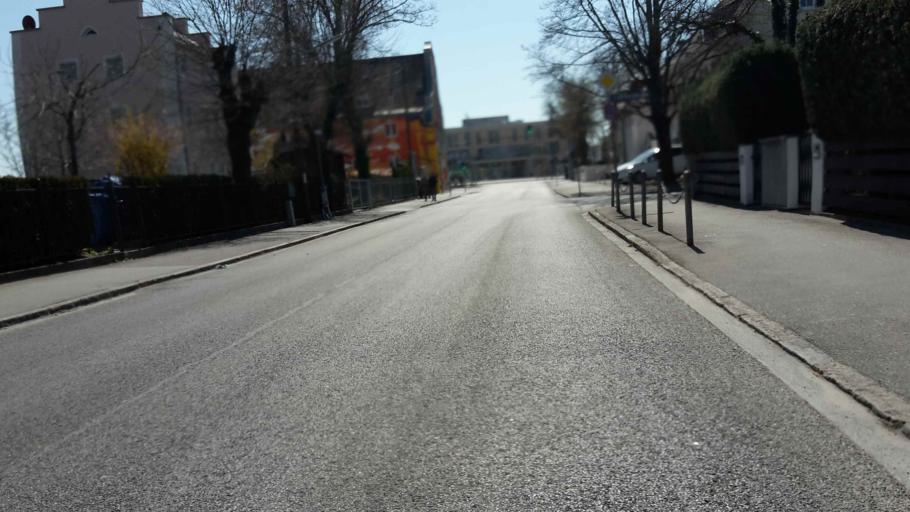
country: DE
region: Bavaria
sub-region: Upper Bavaria
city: Karlsfeld
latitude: 48.1911
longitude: 11.4666
